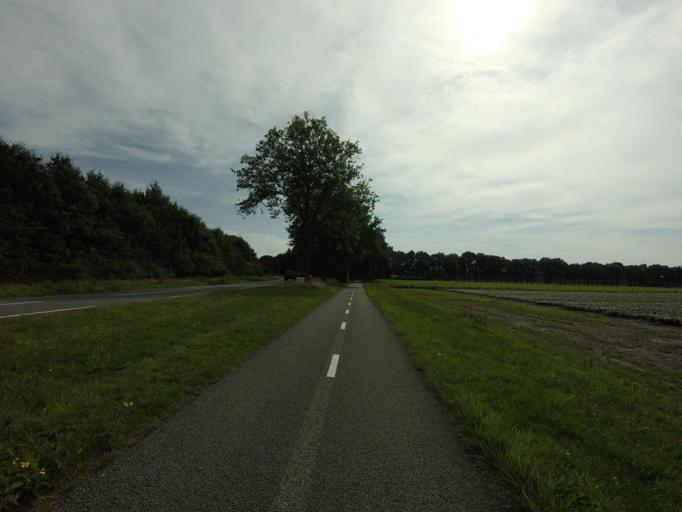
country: NL
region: Drenthe
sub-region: Gemeente Borger-Odoorn
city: Borger
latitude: 52.8741
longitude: 6.7246
